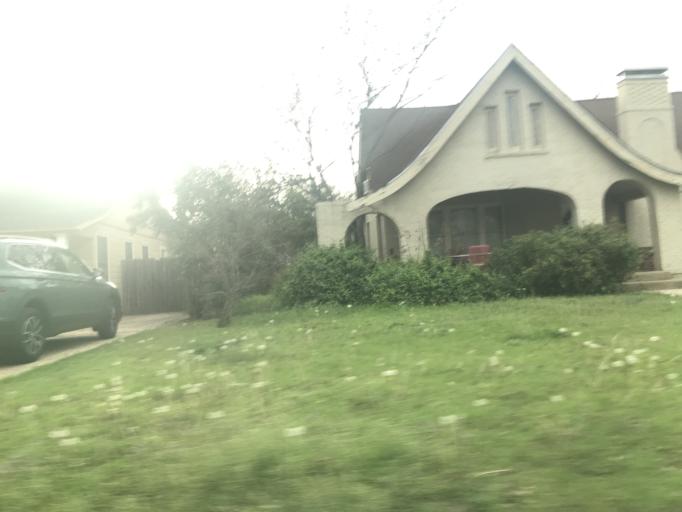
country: US
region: Texas
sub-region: Taylor County
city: Abilene
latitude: 32.4414
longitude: -99.7657
